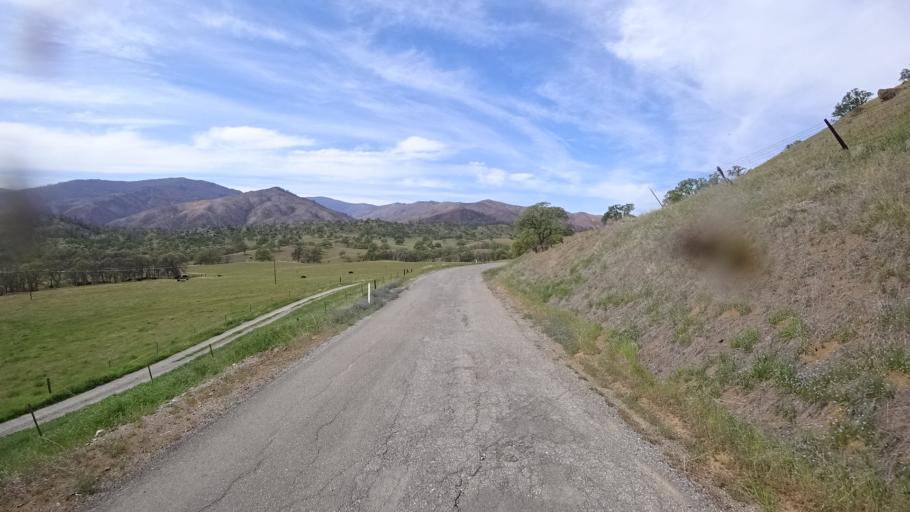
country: US
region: California
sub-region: Glenn County
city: Willows
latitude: 39.6131
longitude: -122.5834
